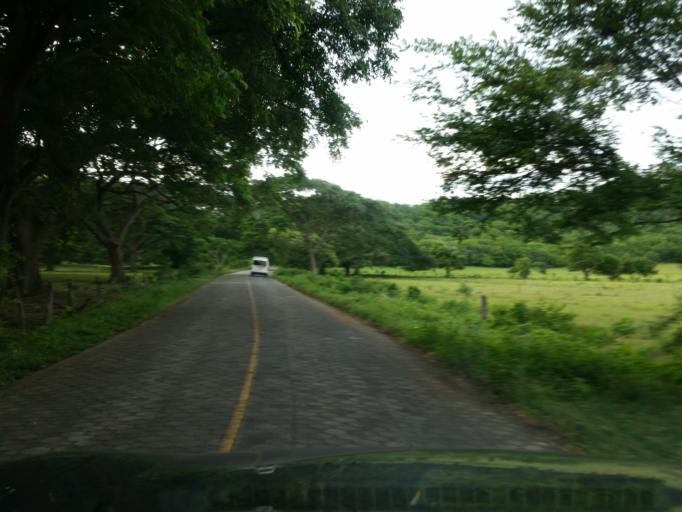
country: NI
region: Rivas
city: San Juan del Sur
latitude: 11.2633
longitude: -85.8679
